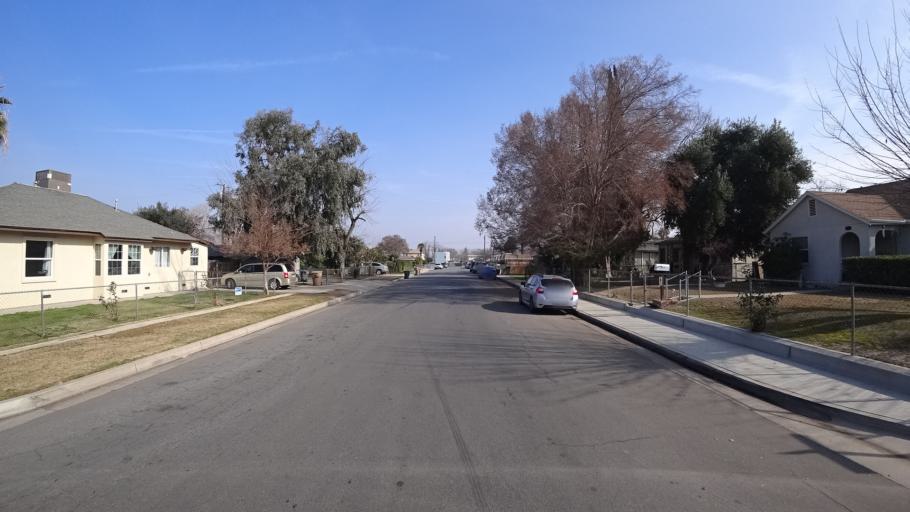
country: US
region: California
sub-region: Kern County
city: Bakersfield
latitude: 35.3599
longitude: -119.0234
